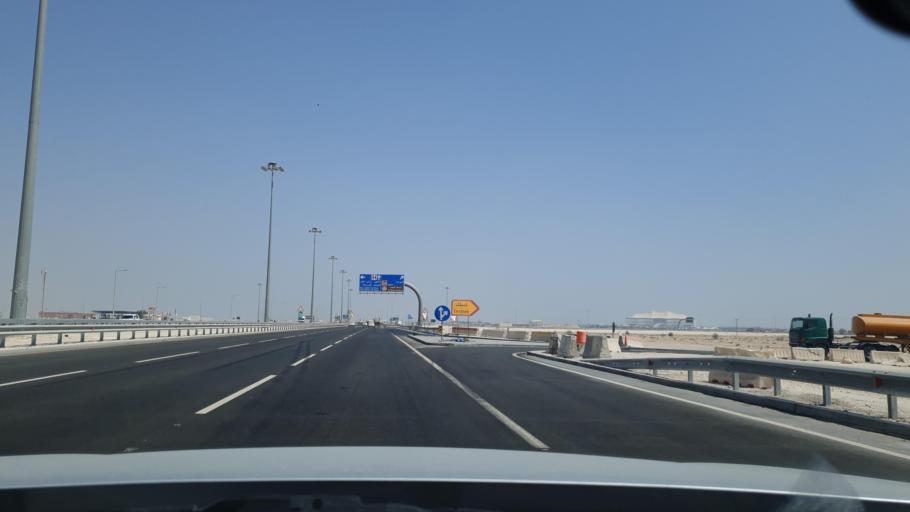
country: QA
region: Al Khawr
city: Al Khawr
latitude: 25.6500
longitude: 51.4509
